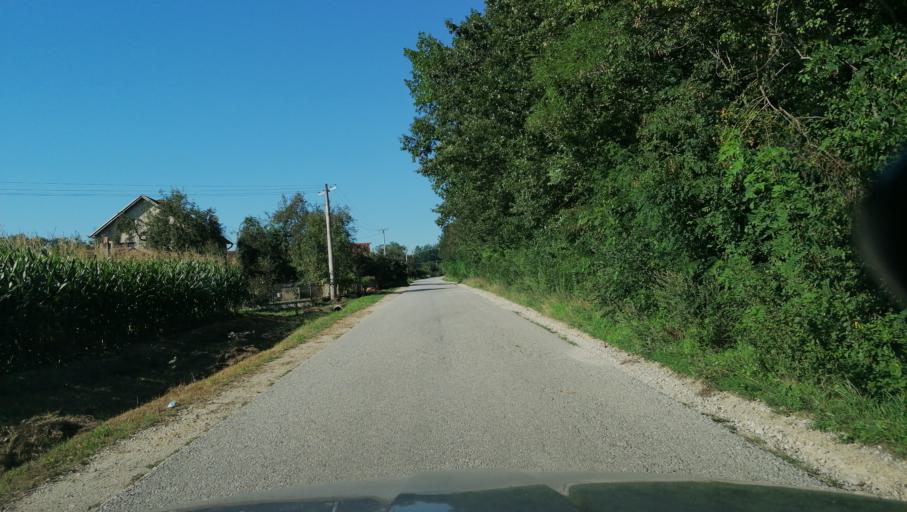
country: RS
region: Central Serbia
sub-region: Sumadijski Okrug
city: Knic
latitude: 43.8612
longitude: 20.6007
